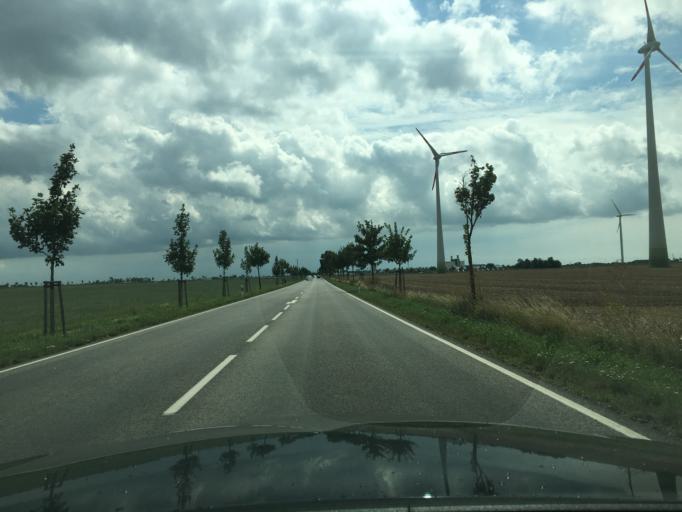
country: DE
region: Saxony-Anhalt
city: Raguhn
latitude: 51.7102
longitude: 12.2492
